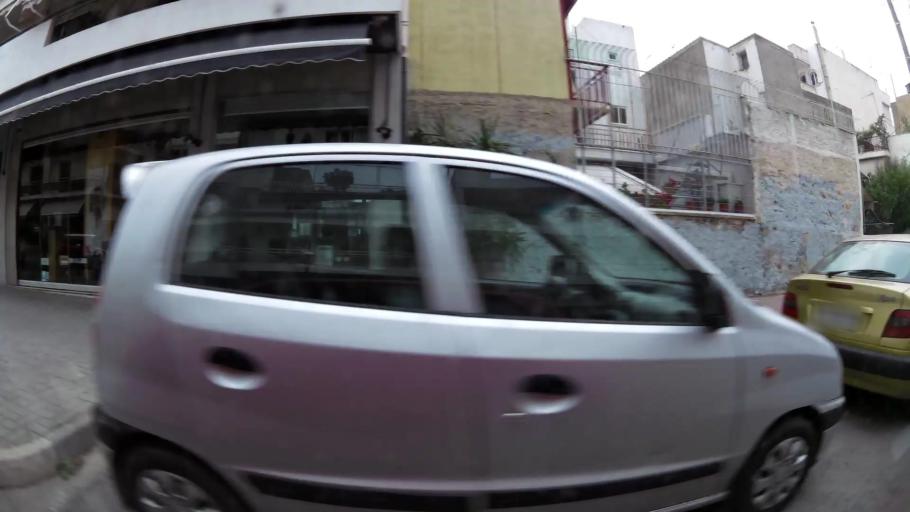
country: GR
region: Attica
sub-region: Nomarchia Athinas
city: Peristeri
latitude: 38.0135
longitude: 23.6924
